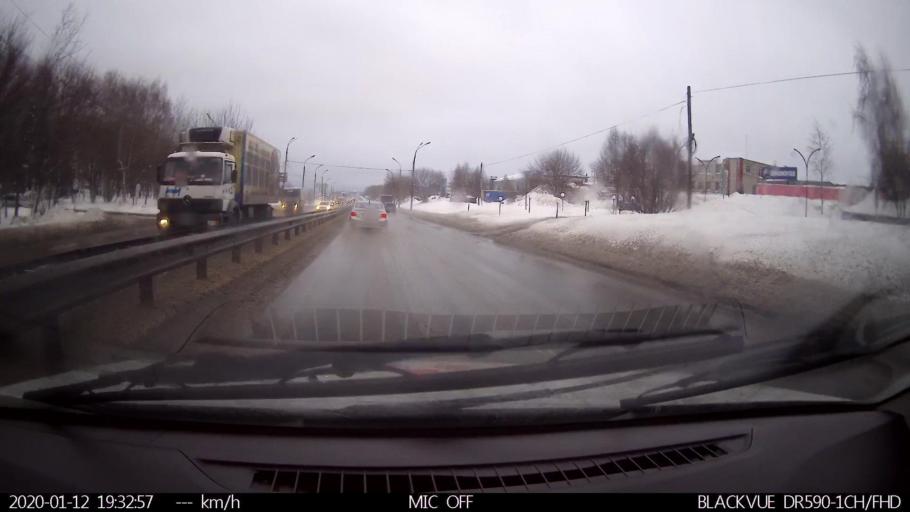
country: RU
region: Nizjnij Novgorod
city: Nizhniy Novgorod
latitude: 56.2401
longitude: 43.9996
